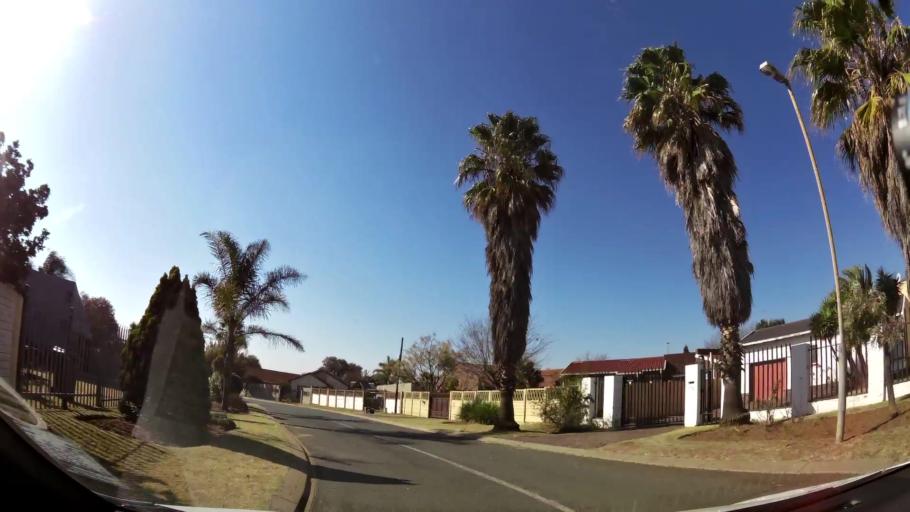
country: ZA
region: Gauteng
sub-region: Ekurhuleni Metropolitan Municipality
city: Germiston
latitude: -26.2442
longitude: 28.1079
